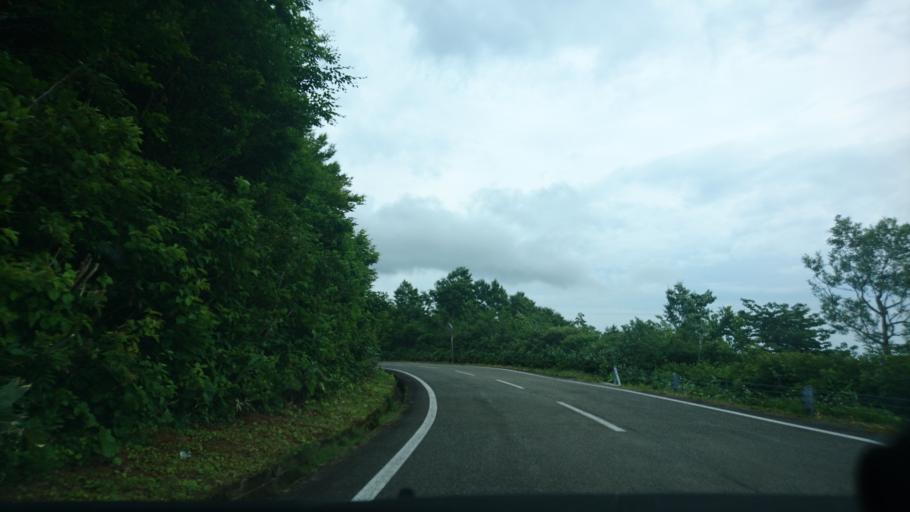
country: JP
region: Akita
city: Yuzawa
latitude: 39.1548
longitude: 140.7534
